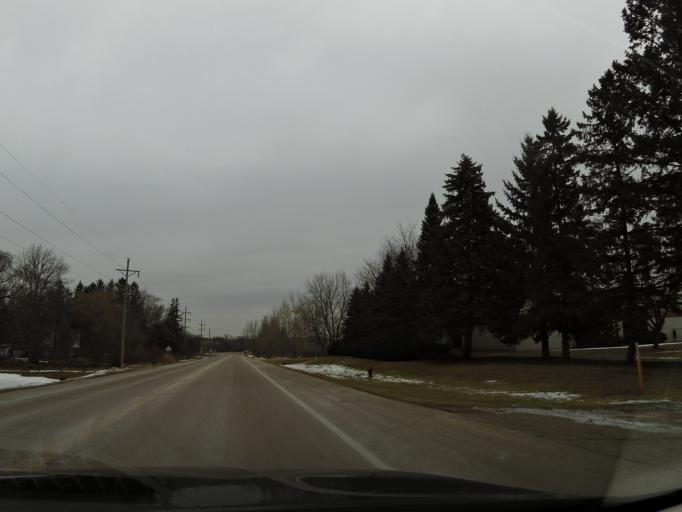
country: US
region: Minnesota
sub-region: Carver County
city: Watertown
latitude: 44.9545
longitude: -93.8386
